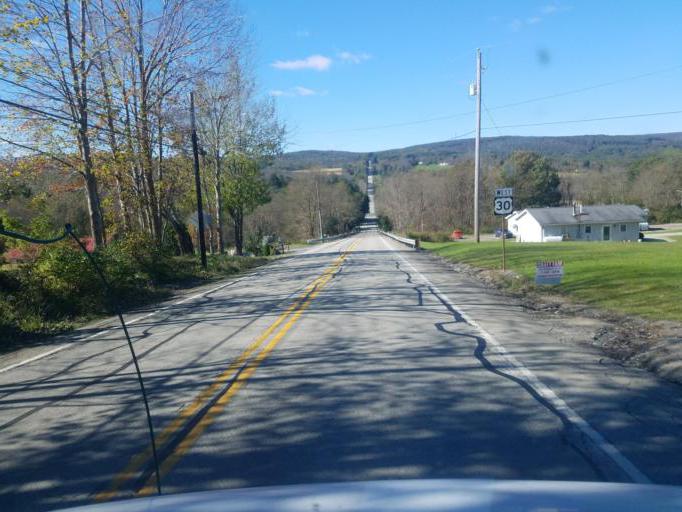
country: US
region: Pennsylvania
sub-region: Somerset County
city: Boswell
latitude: 40.1647
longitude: -79.0842
